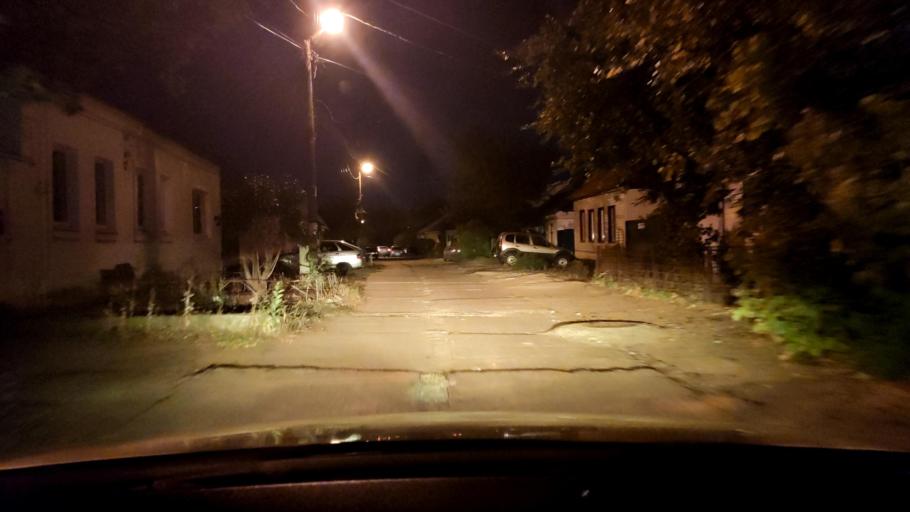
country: RU
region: Voronezj
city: Voronezh
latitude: 51.6815
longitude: 39.1600
